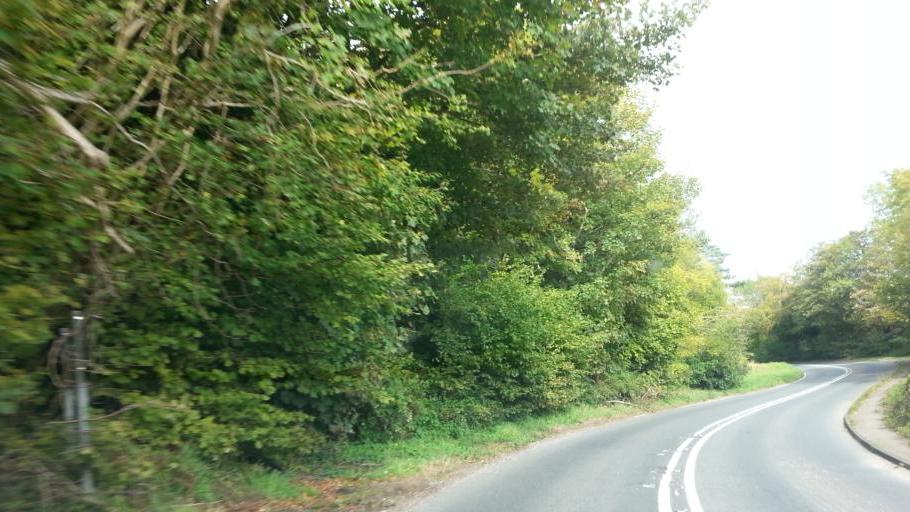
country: GB
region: England
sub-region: Gloucestershire
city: Painswick
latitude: 51.8030
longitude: -2.1918
